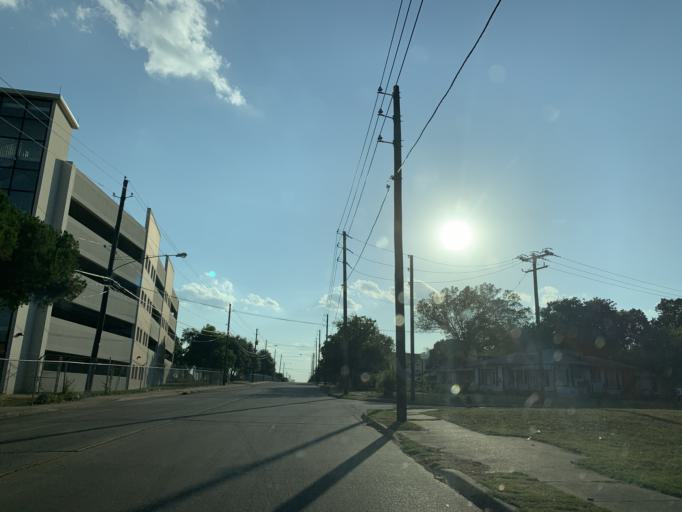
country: US
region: Texas
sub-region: Dallas County
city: Dallas
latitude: 32.6979
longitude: -96.7885
